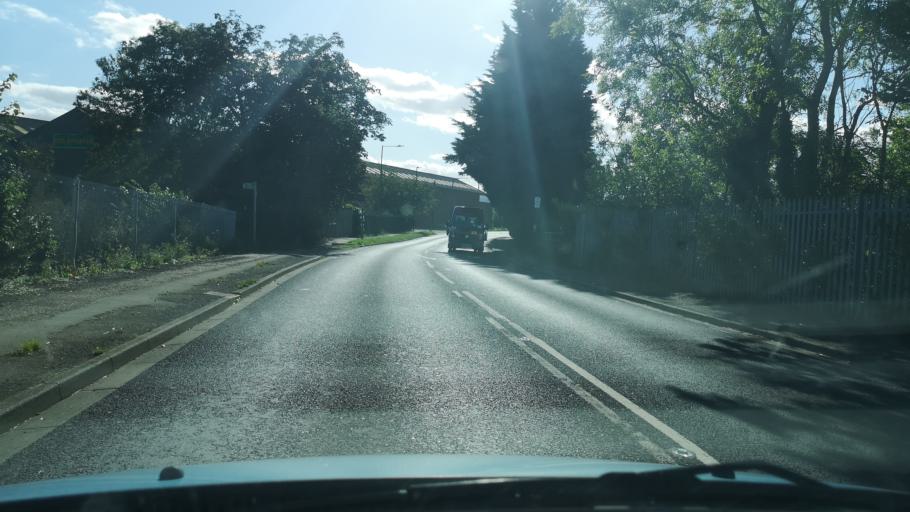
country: GB
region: England
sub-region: Doncaster
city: Bentley
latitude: 53.5511
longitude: -1.1337
